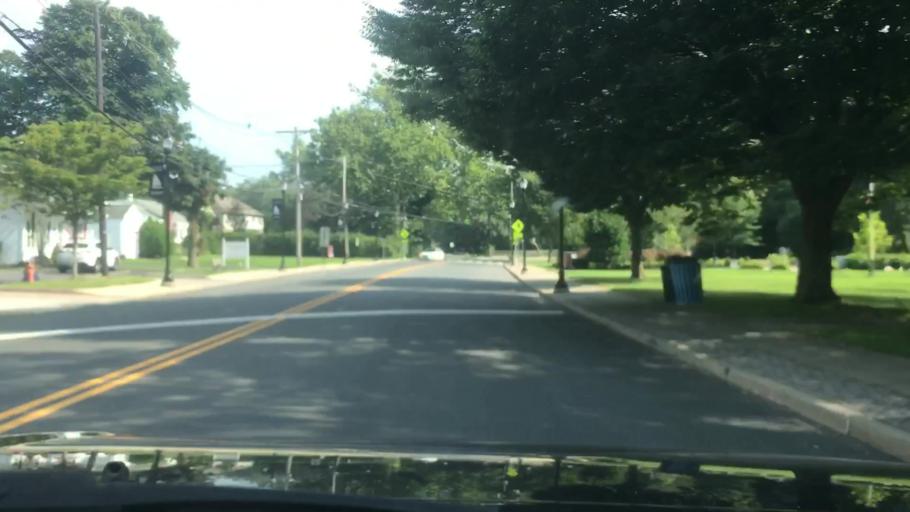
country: US
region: New Jersey
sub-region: Monmouth County
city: Little Silver
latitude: 40.3373
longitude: -74.0402
